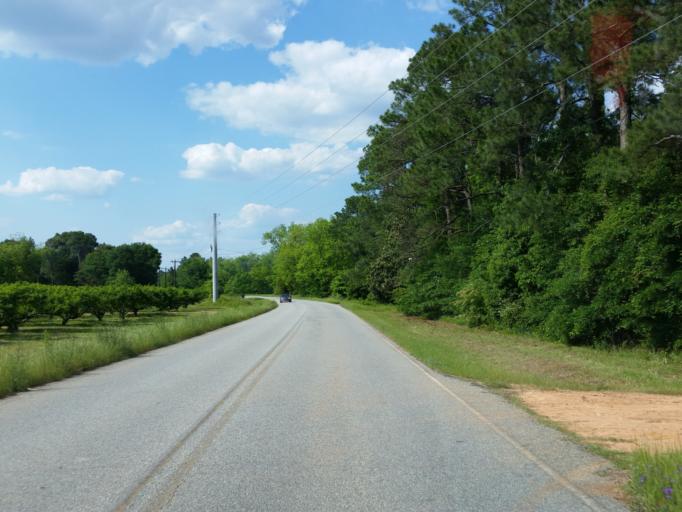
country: US
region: Georgia
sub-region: Peach County
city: Byron
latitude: 32.5809
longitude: -83.7486
